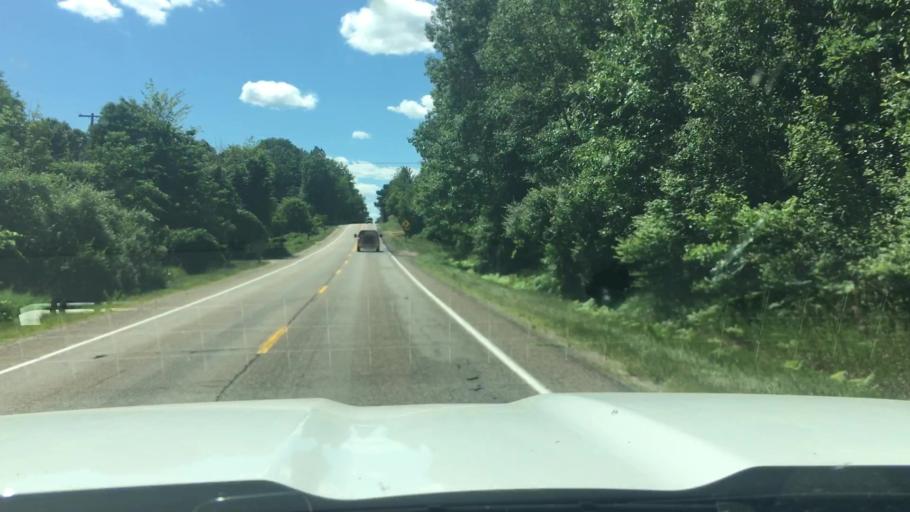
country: US
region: Michigan
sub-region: Kent County
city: Cedar Springs
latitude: 43.1755
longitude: -85.5876
